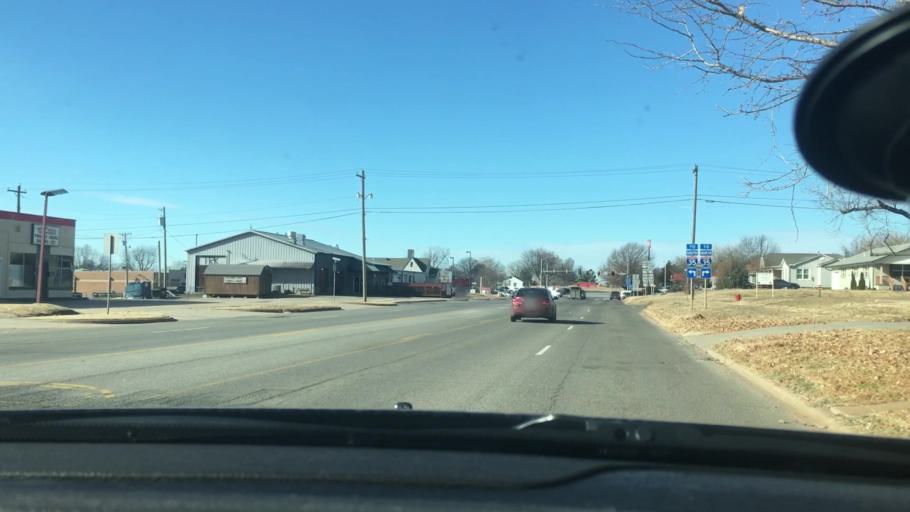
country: US
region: Oklahoma
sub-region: McClain County
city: Purcell
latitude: 35.0138
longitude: -97.3634
